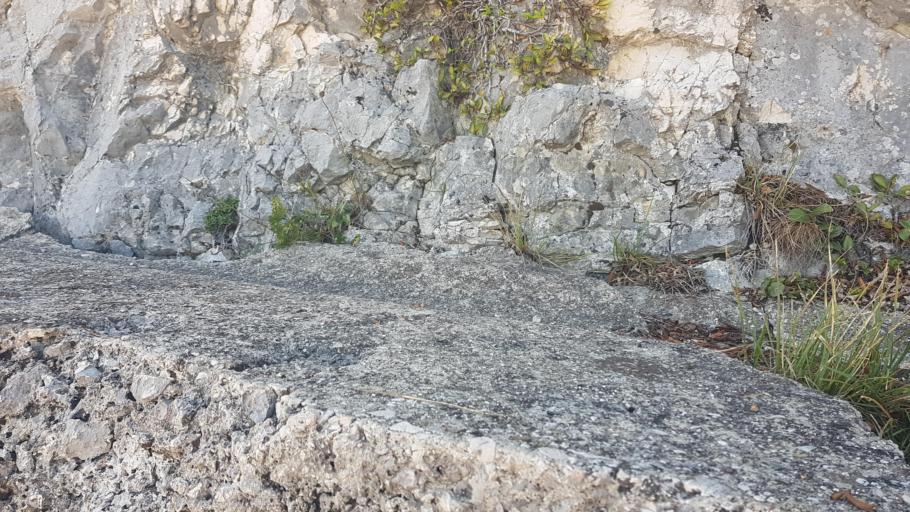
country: IT
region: Trentino-Alto Adige
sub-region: Provincia di Trento
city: Cadine
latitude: 46.1000
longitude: 11.0849
